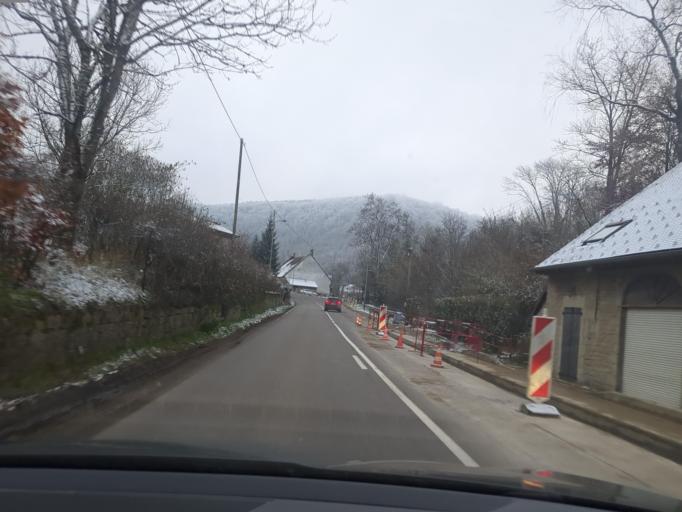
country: FR
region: Franche-Comte
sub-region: Departement du Jura
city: Perrigny
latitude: 46.6422
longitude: 5.6018
